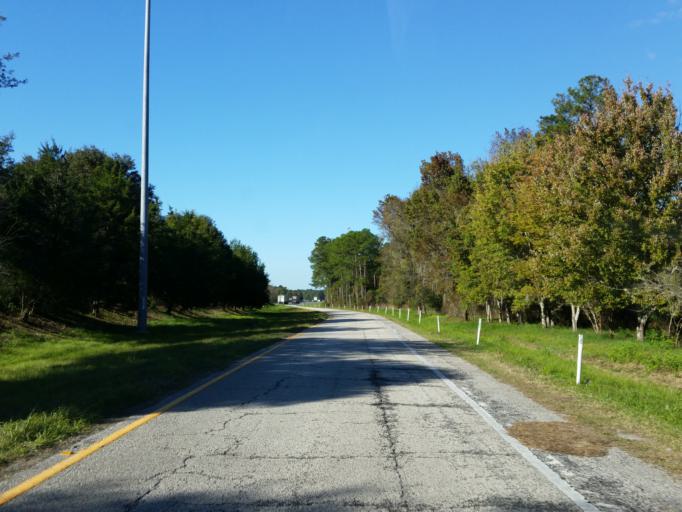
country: US
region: Florida
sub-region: Alachua County
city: Gainesville
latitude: 29.4984
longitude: -82.2949
